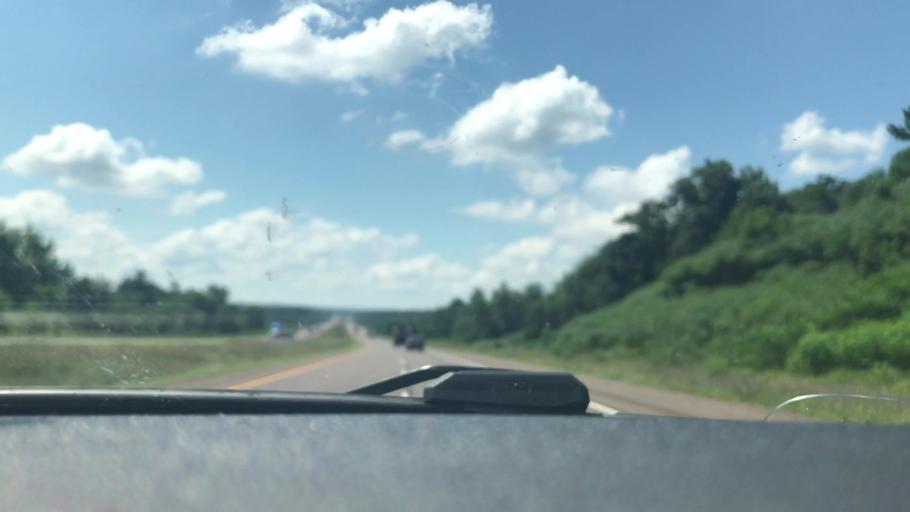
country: US
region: Wisconsin
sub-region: Chippewa County
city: Chippewa Falls
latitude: 44.9337
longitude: -91.4285
